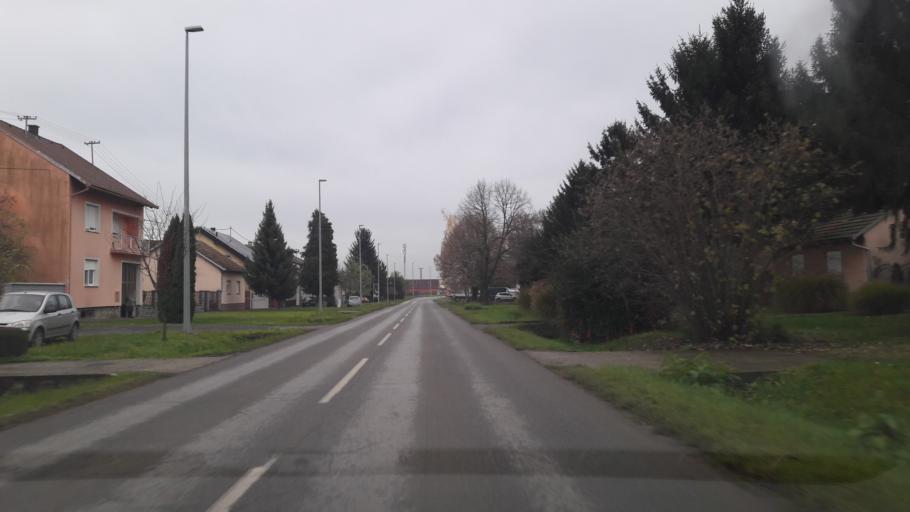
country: HR
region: Osjecko-Baranjska
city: Josipovac
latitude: 45.5811
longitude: 18.5841
